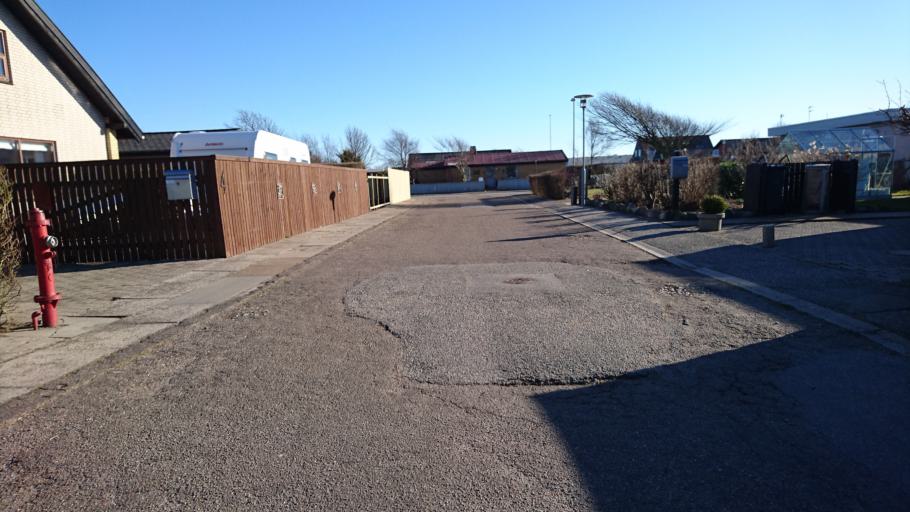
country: DK
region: North Denmark
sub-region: Frederikshavn Kommune
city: Skagen
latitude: 57.7310
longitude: 10.5762
